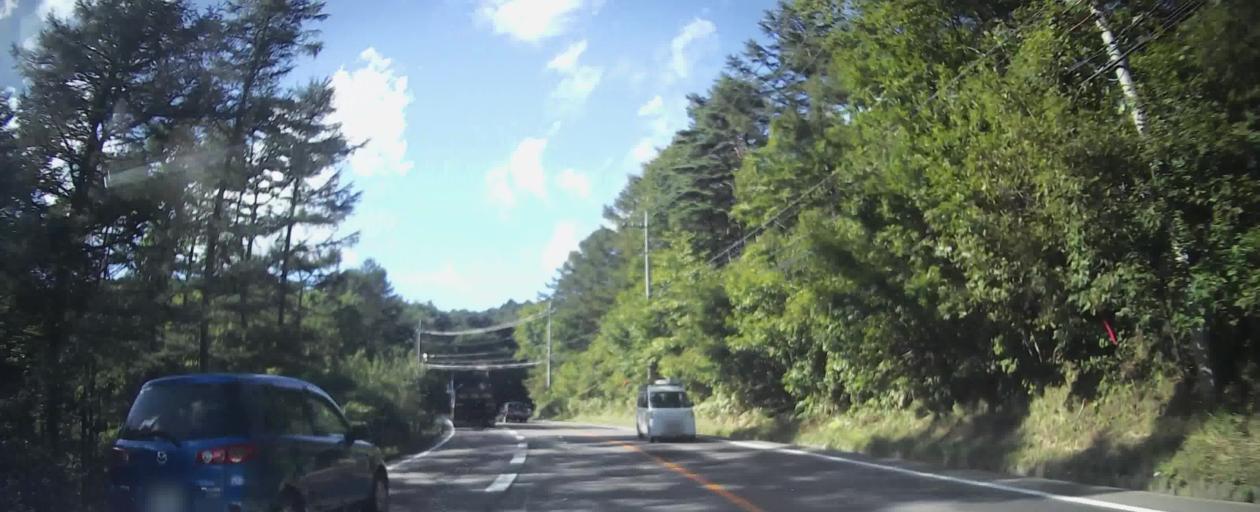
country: JP
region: Gunma
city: Nakanojomachi
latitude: 36.6030
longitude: 138.5847
